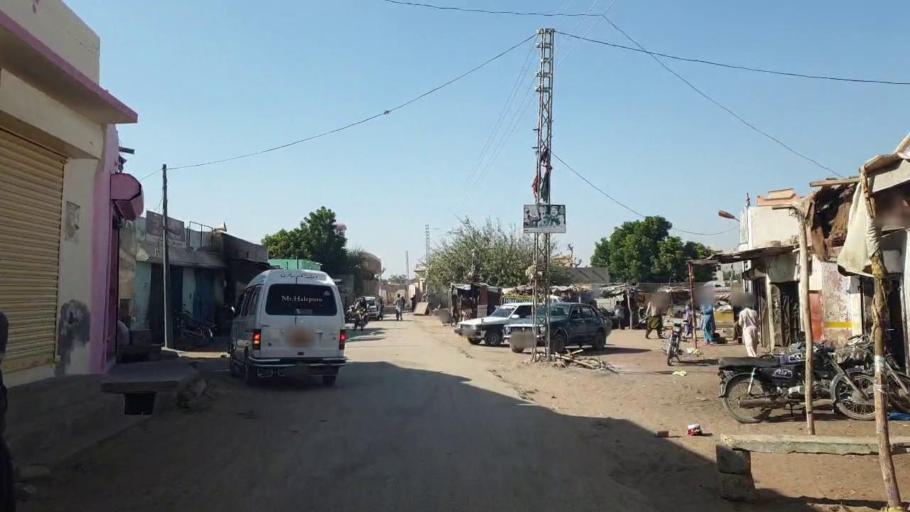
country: PK
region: Sindh
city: Jamshoro
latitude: 25.4100
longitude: 67.7853
